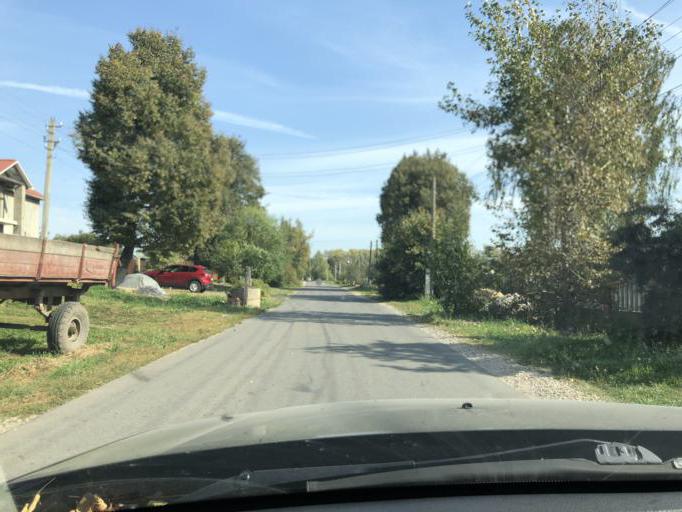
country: RU
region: Tula
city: Yasnogorsk
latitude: 54.4854
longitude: 37.6891
